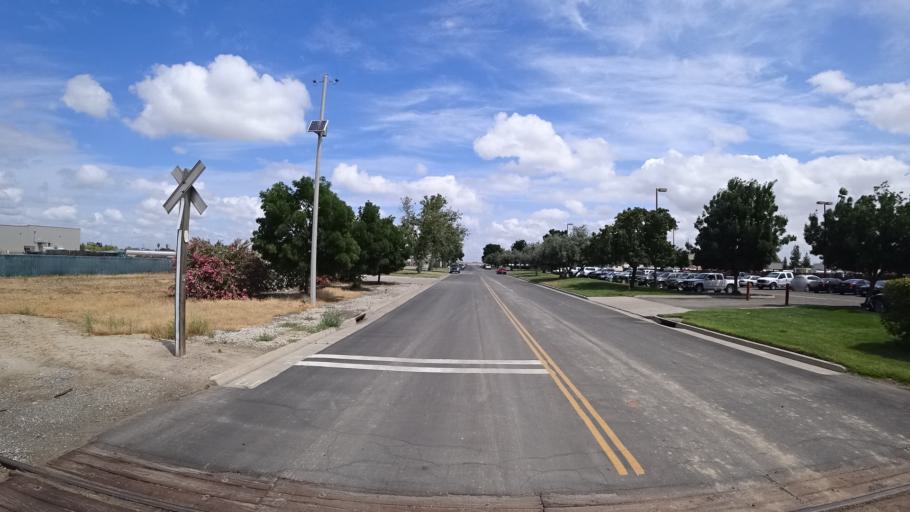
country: US
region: California
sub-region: Kings County
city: Home Garden
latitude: 36.2803
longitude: -119.6506
